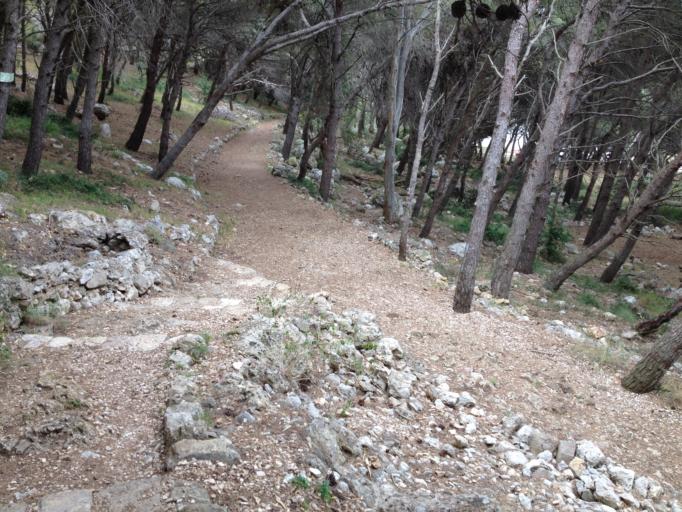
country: IT
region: Apulia
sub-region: Provincia di Lecce
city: Nardo
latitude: 40.1428
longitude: 17.9779
